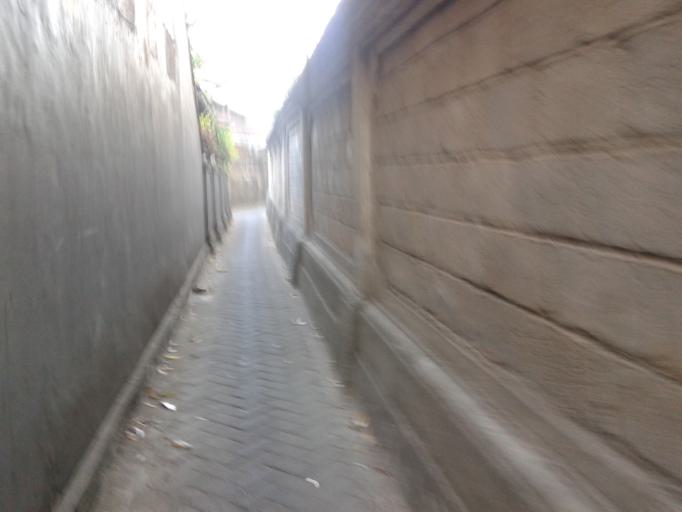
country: ID
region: Bali
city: Kuta
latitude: -8.7068
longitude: 115.1743
